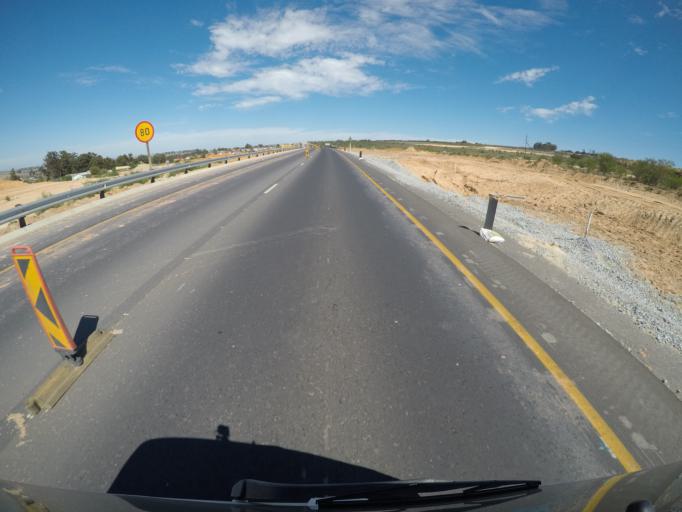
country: ZA
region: Western Cape
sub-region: West Coast District Municipality
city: Malmesbury
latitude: -33.4863
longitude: 18.6733
